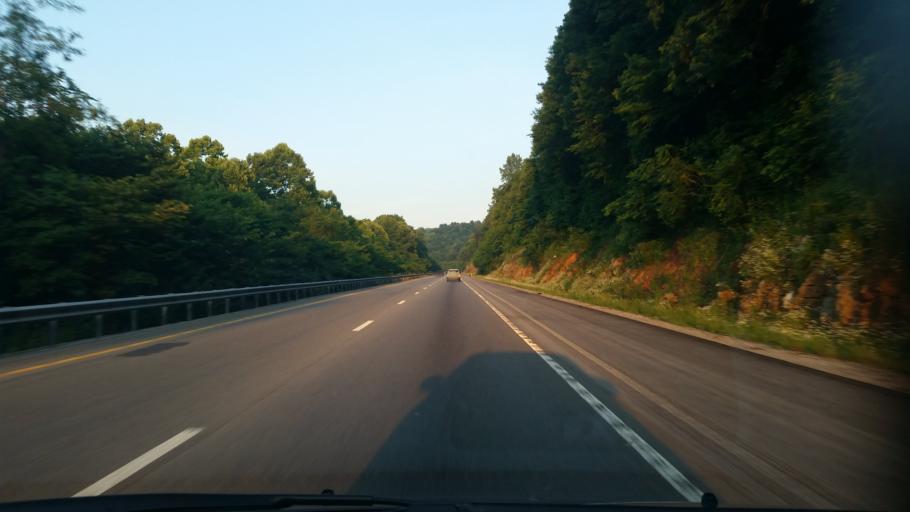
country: US
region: Tennessee
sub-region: Putnam County
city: Algood
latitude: 36.1443
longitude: -85.4003
